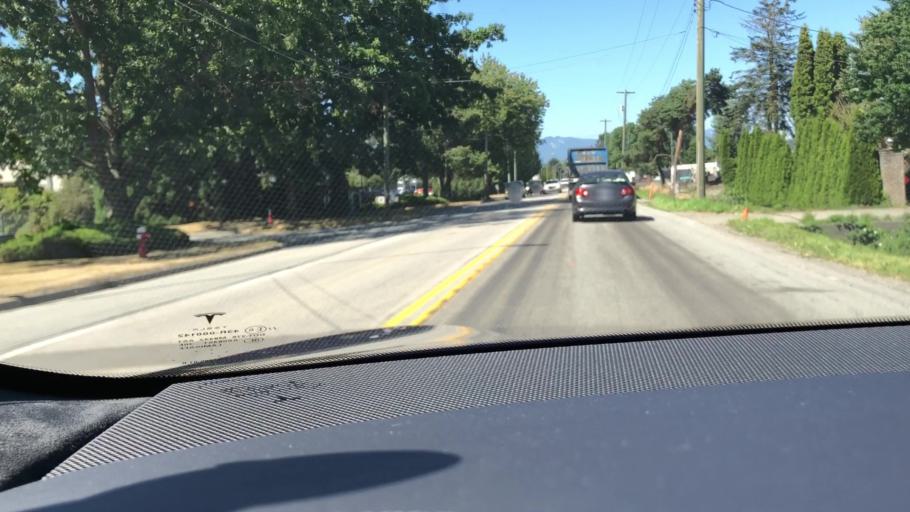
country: CA
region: British Columbia
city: Richmond
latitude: 49.1858
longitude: -123.0691
